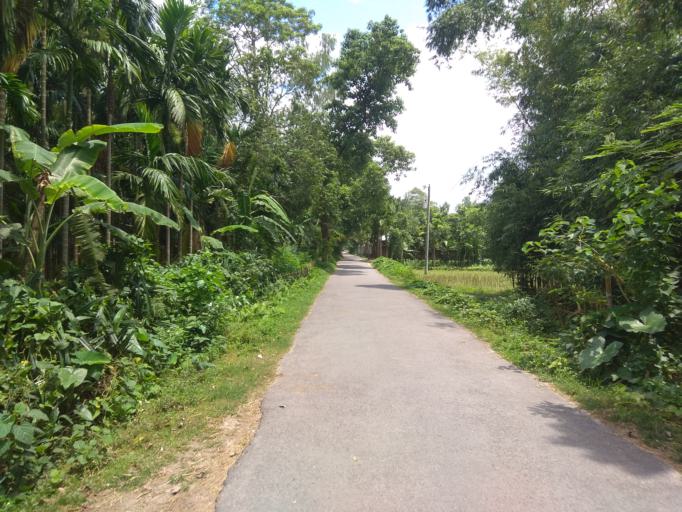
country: IN
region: West Bengal
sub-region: Koch Bihar
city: Haldibari
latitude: 26.1640
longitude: 88.9238
